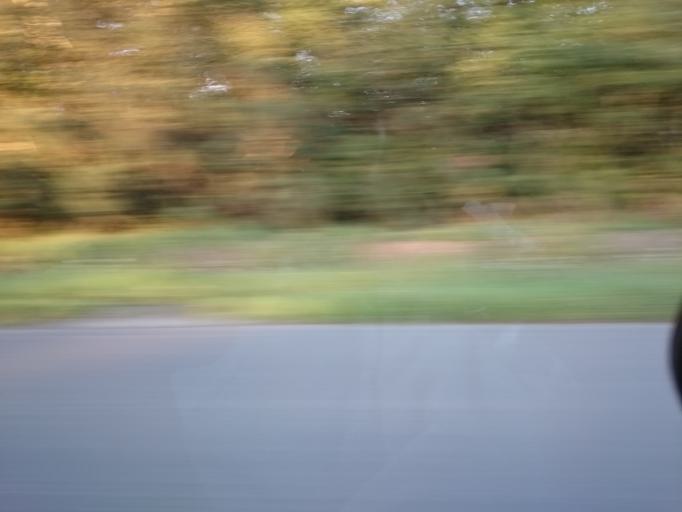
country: FR
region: Brittany
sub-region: Departement du Finistere
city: Morlaix
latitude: 48.5873
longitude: -3.7860
